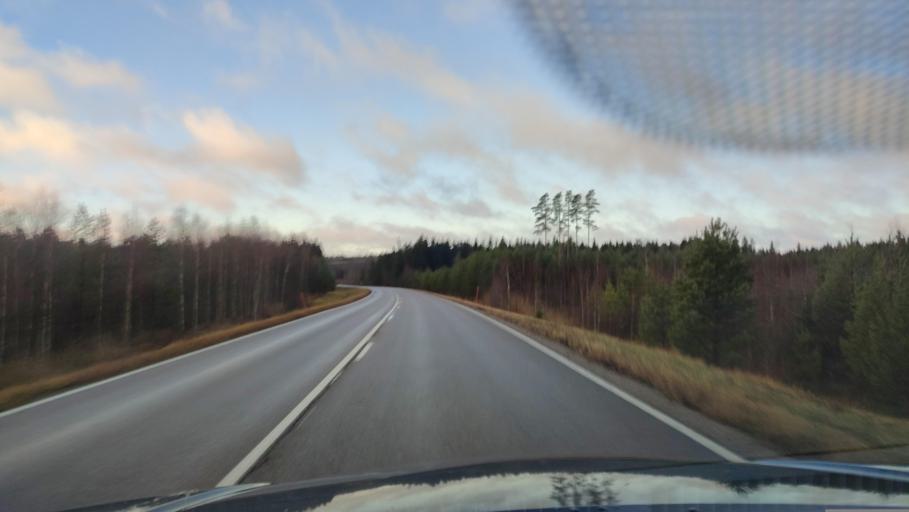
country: FI
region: Ostrobothnia
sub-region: Sydosterbotten
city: Kristinestad
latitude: 62.2996
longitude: 21.3963
